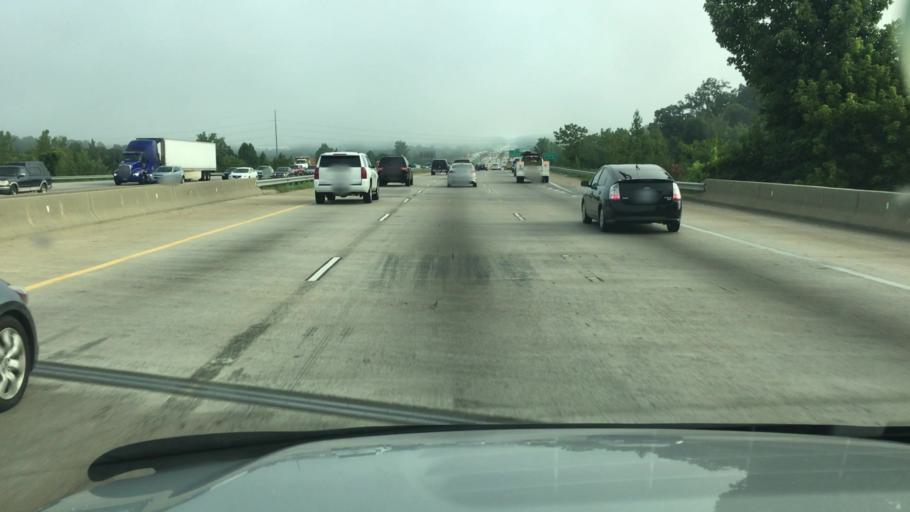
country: US
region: North Carolina
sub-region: Gaston County
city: Belmont
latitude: 35.2269
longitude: -80.9708
